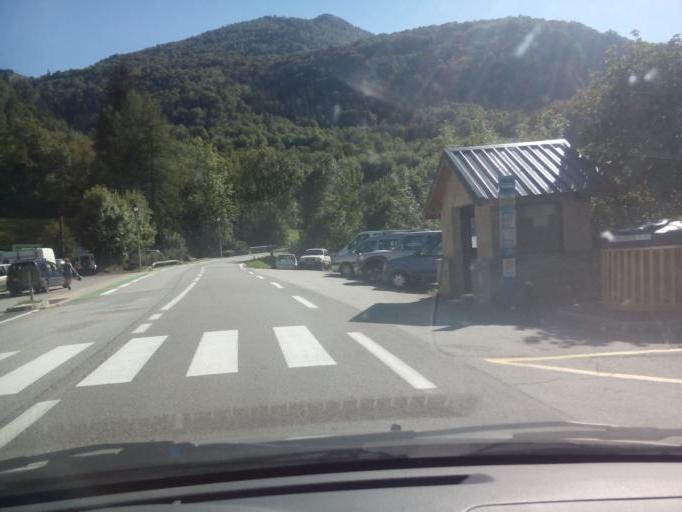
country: FR
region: Rhone-Alpes
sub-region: Departement de l'Isere
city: Mont-de-Lans
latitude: 45.0438
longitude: 6.1247
